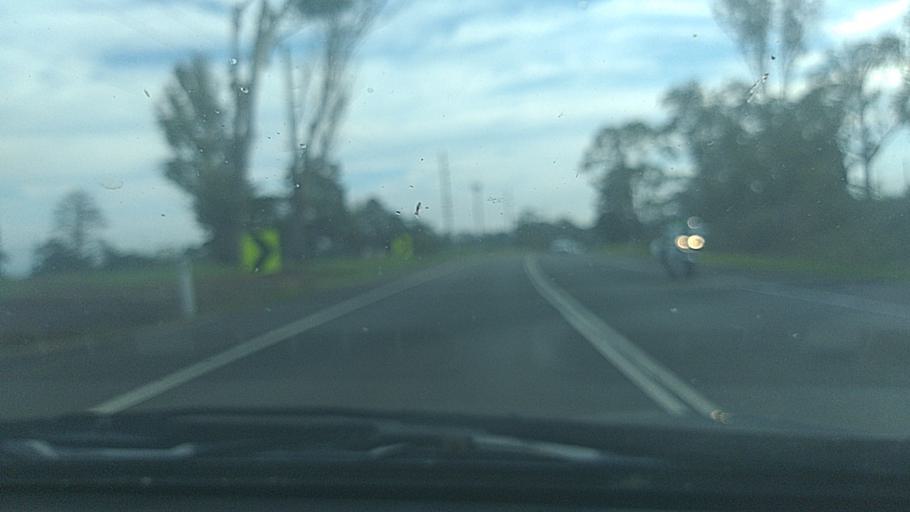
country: AU
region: New South Wales
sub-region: Penrith Municipality
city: Glenmore Park
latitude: -33.8161
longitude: 150.6888
